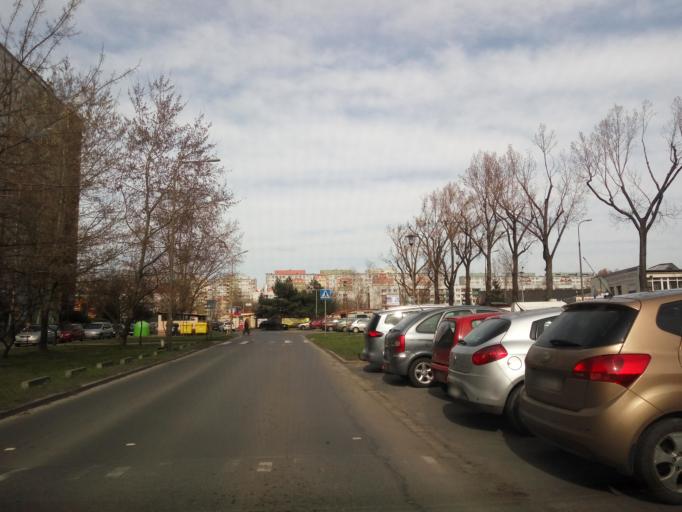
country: PL
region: Lower Silesian Voivodeship
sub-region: Powiat wroclawski
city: Wroclaw
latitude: 51.0812
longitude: 17.0411
